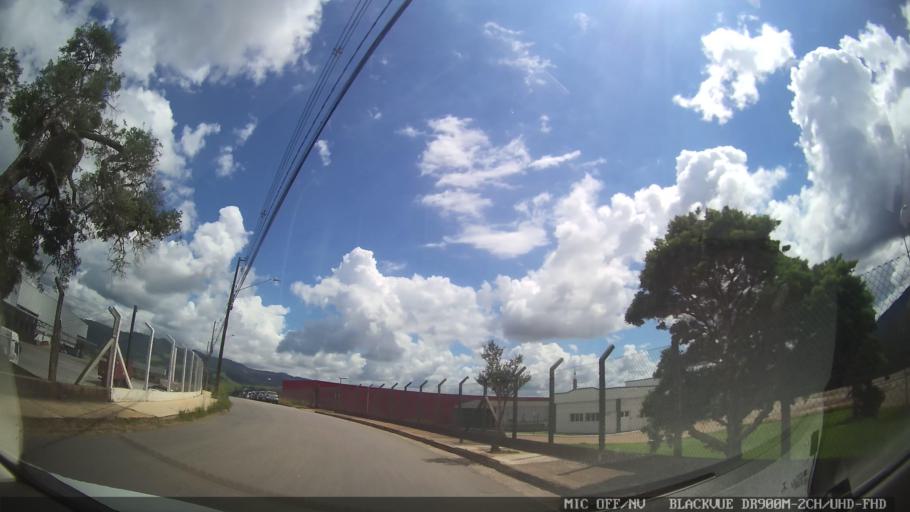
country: BR
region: Minas Gerais
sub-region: Extrema
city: Extrema
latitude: -22.8750
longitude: -46.3493
